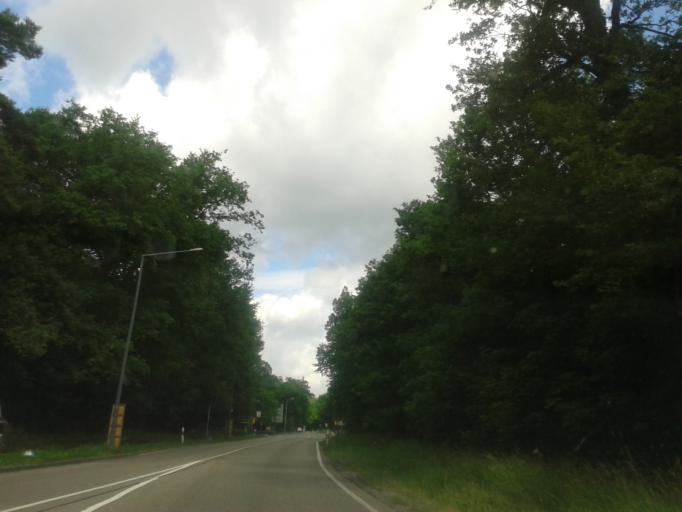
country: DE
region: Saxony
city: Radebeul
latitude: 51.1033
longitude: 13.7117
